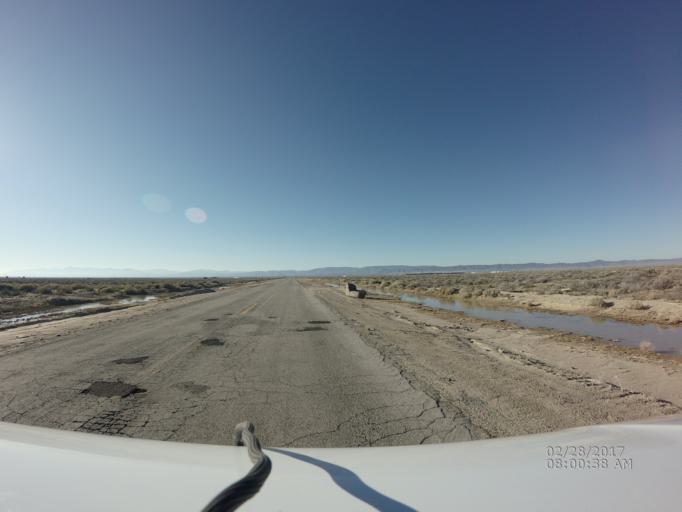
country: US
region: California
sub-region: Los Angeles County
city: Lancaster
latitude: 34.7673
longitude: -118.1845
